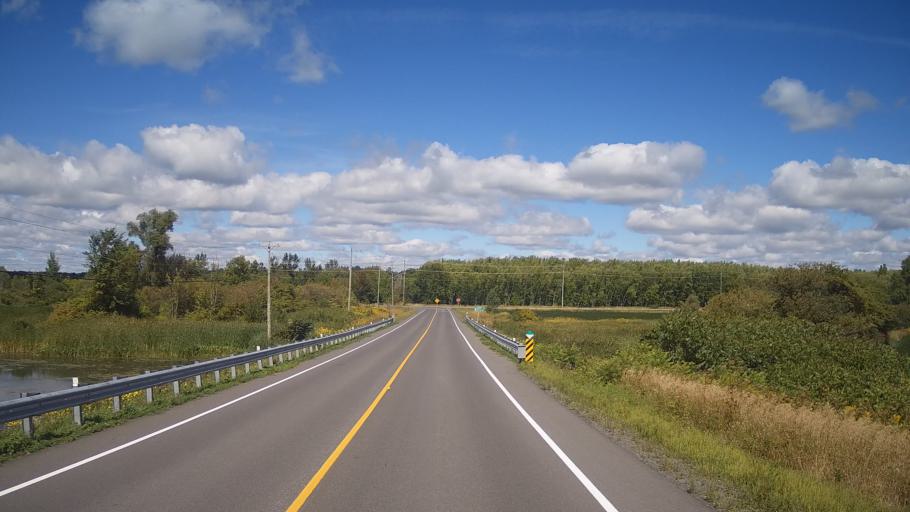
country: US
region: New York
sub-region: St. Lawrence County
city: Ogdensburg
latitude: 44.8613
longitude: -75.2755
